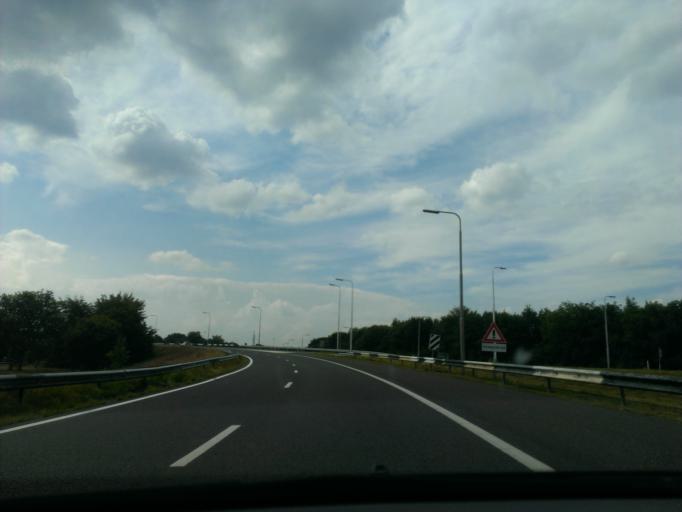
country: NL
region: North Holland
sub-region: Gemeente Laren
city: Laren
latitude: 52.2341
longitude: 5.2401
